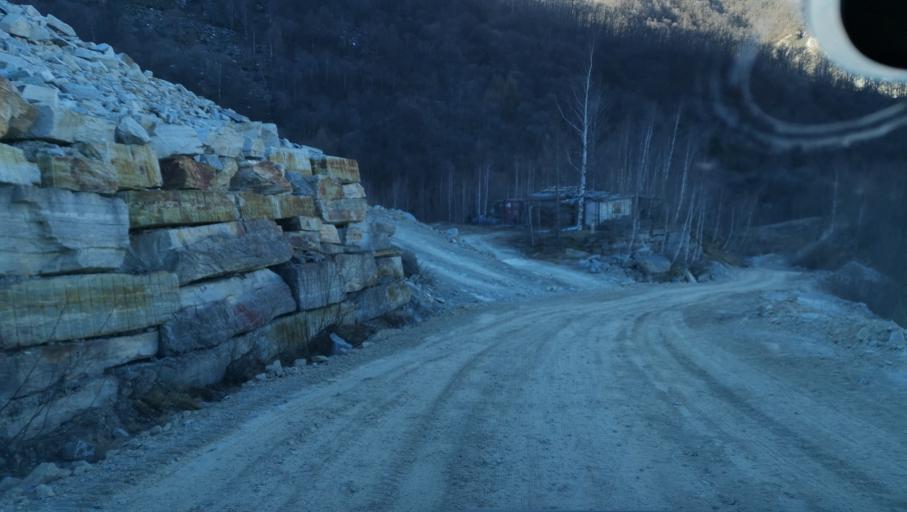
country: IT
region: Piedmont
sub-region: Provincia di Torino
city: Rora
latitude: 44.7572
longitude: 7.1982
